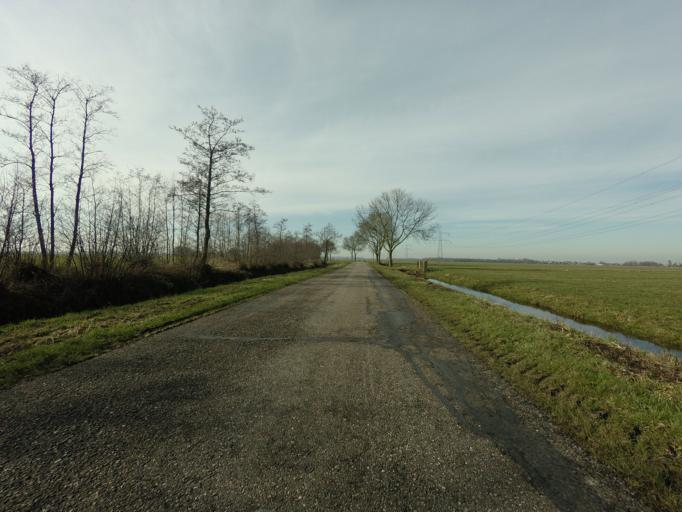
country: NL
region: South Holland
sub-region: Gemeente Sliedrecht
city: Sliedrecht
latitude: 51.8588
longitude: 4.7833
